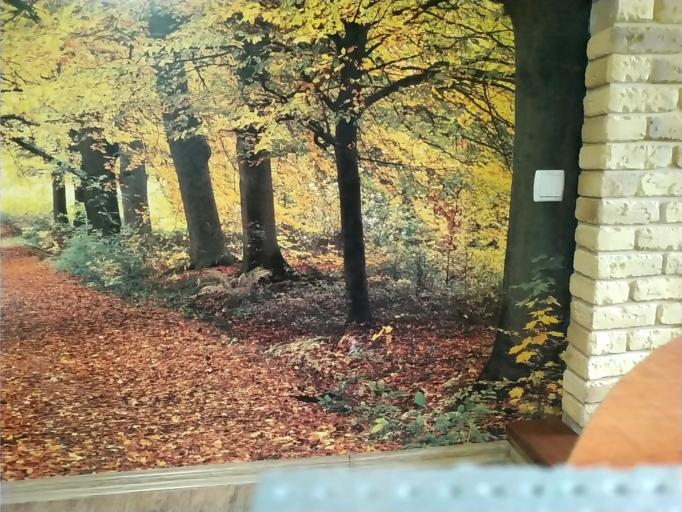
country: RU
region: Tverskaya
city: Staritsa
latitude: 56.4899
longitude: 35.2617
